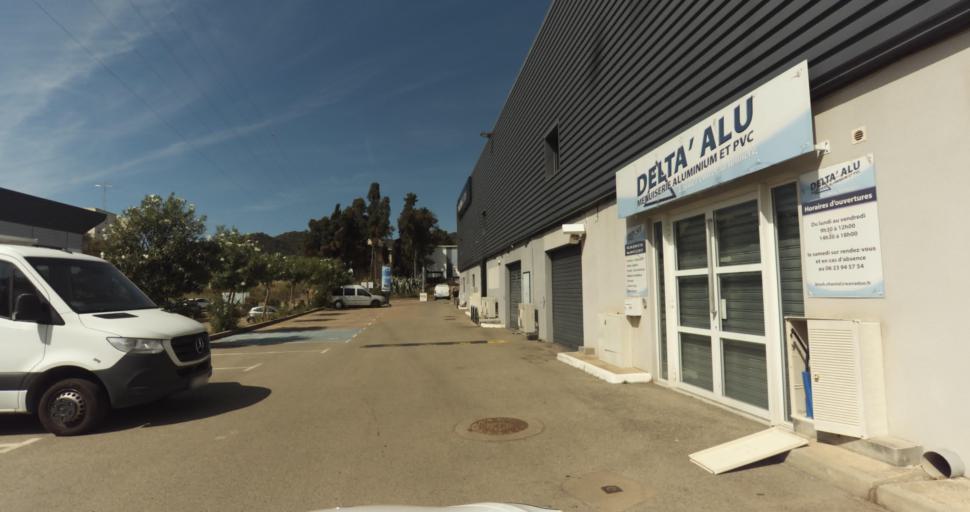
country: FR
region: Corsica
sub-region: Departement de la Corse-du-Sud
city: Ajaccio
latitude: 41.9472
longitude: 8.7644
